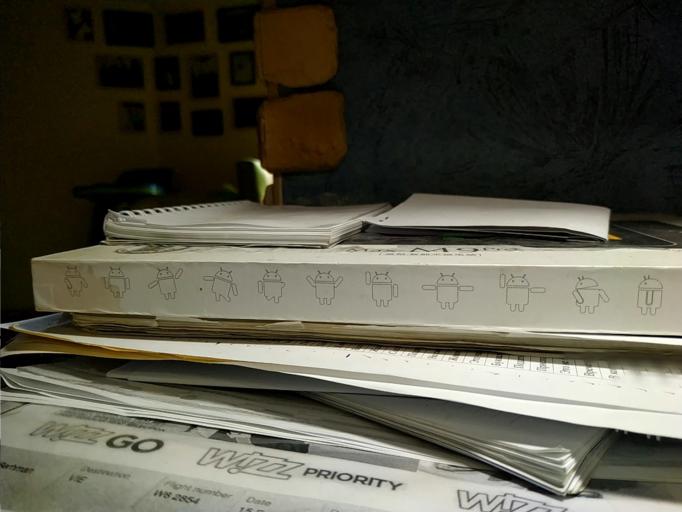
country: RU
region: Novgorod
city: Poddor'ye
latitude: 57.5297
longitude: 30.9046
